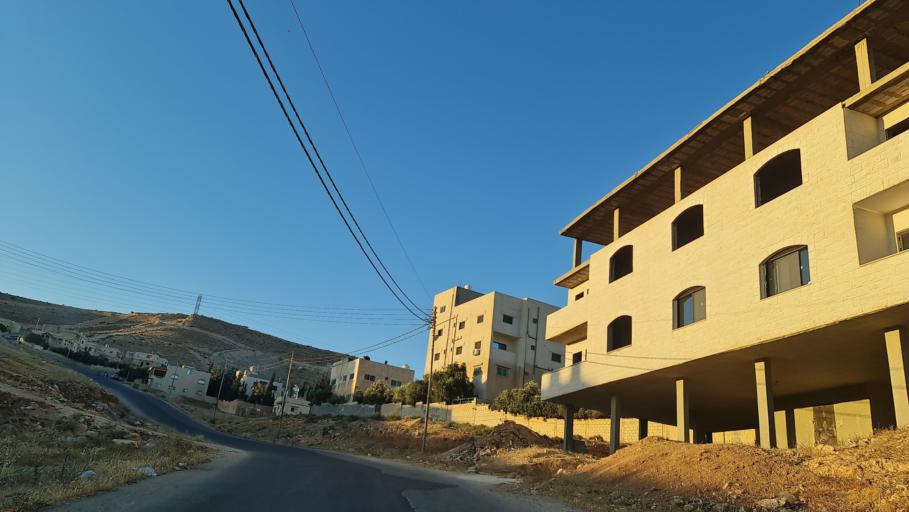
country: JO
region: Zarqa
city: Zarqa
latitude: 32.0877
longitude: 36.0178
